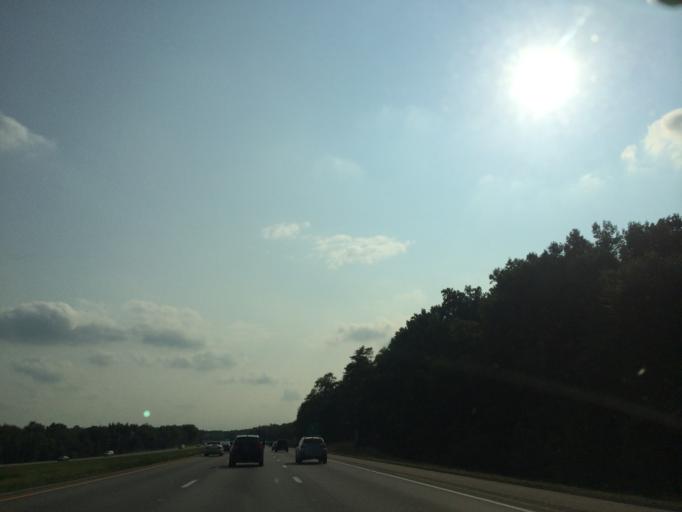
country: US
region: Pennsylvania
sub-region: Cumberland County
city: Enola
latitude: 40.3033
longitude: -76.9663
